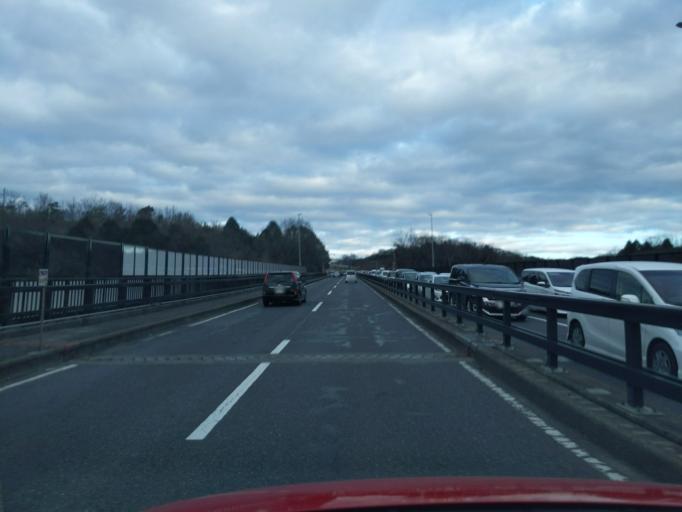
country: JP
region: Gifu
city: Tajimi
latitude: 35.3412
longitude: 137.1393
